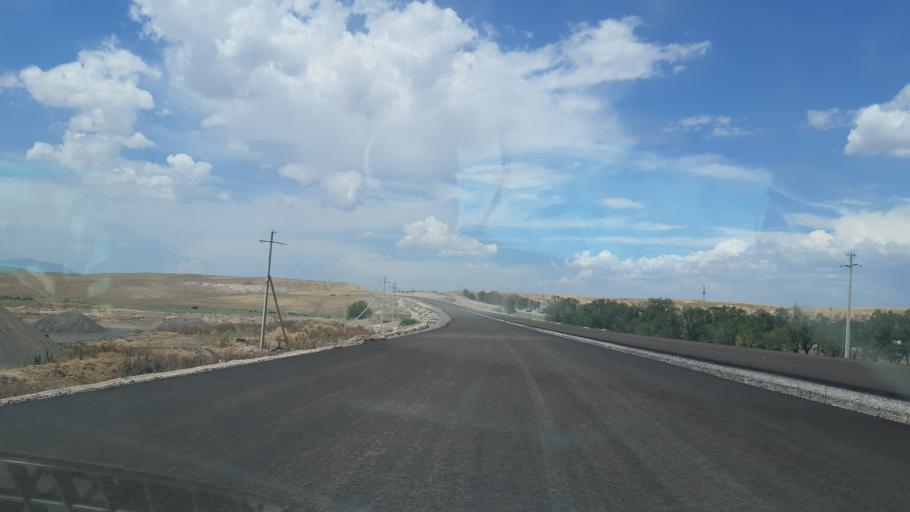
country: KG
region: Chuy
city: Bystrovka
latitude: 43.3206
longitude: 76.0639
